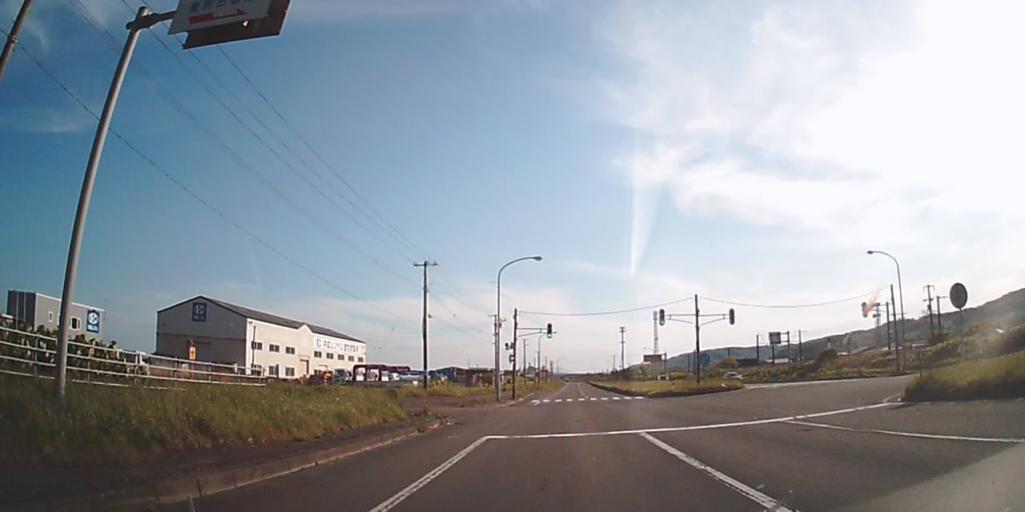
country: JP
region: Hokkaido
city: Muroran
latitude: 42.4029
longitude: 141.0994
